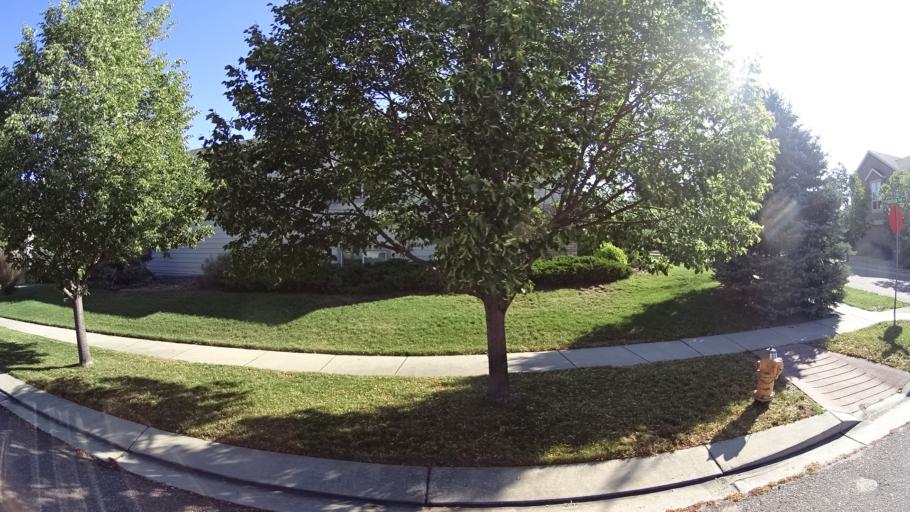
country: US
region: Colorado
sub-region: El Paso County
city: Black Forest
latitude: 38.9799
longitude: -104.7622
